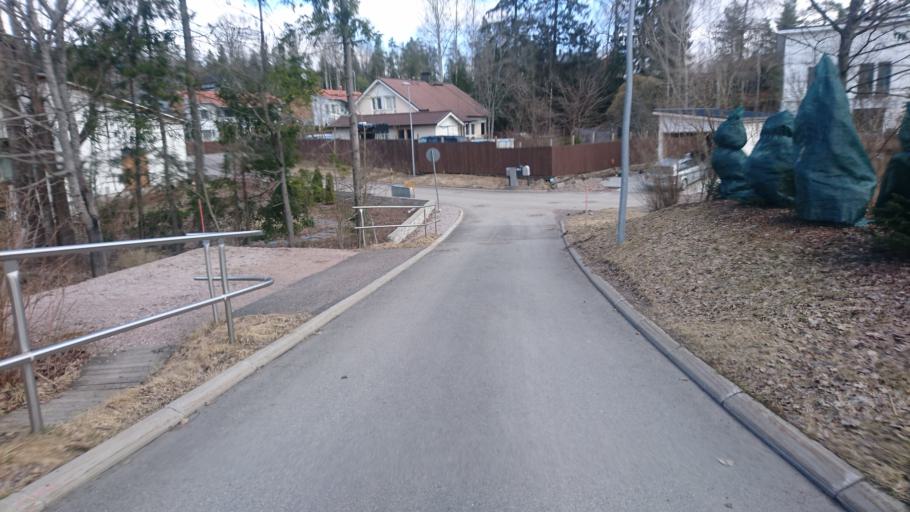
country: FI
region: Uusimaa
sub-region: Helsinki
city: Kauniainen
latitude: 60.1989
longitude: 24.7179
